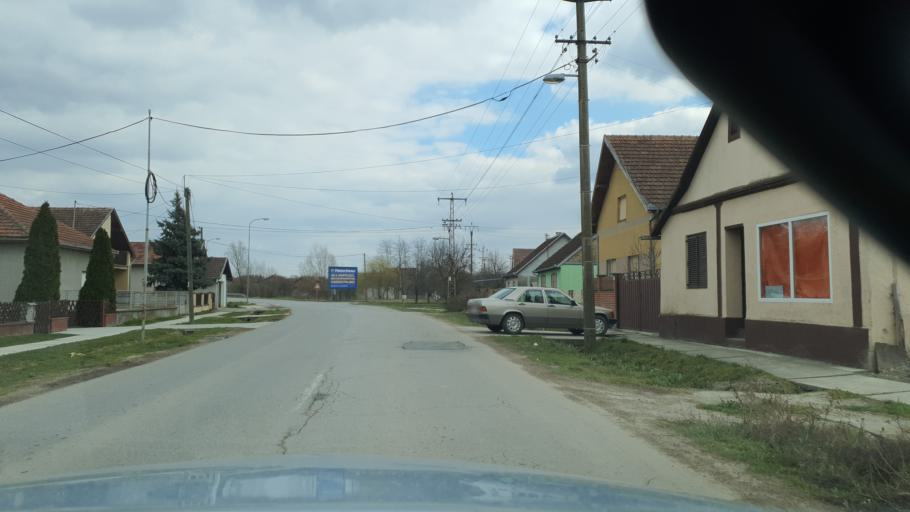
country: RS
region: Autonomna Pokrajina Vojvodina
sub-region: Juznobacki Okrug
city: Bac
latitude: 45.3868
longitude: 19.2282
